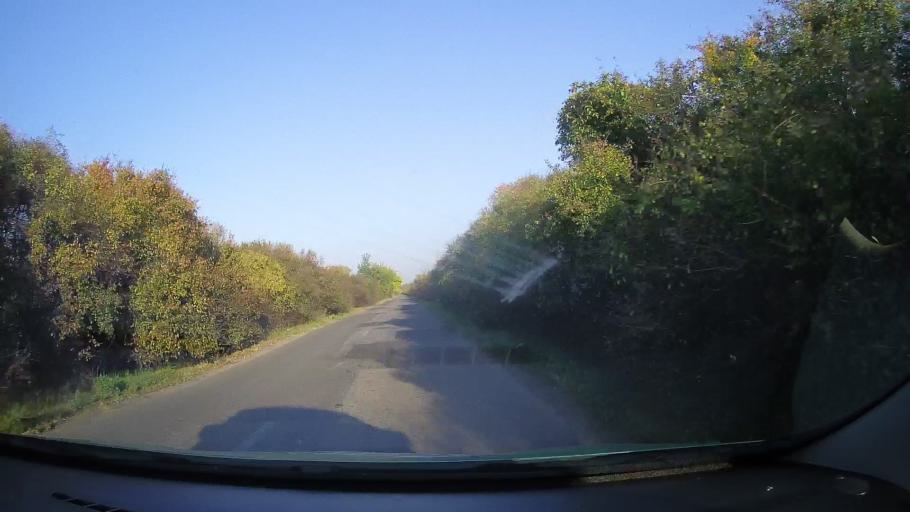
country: RO
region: Arad
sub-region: Comuna Tarnova
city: Tarnova
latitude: 46.3197
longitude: 21.8093
